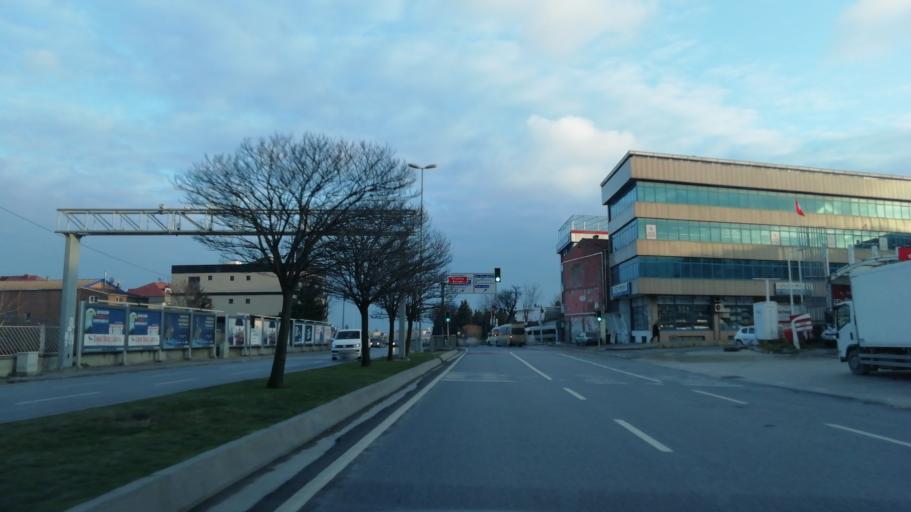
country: TR
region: Istanbul
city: Yakuplu
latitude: 40.9911
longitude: 28.7187
